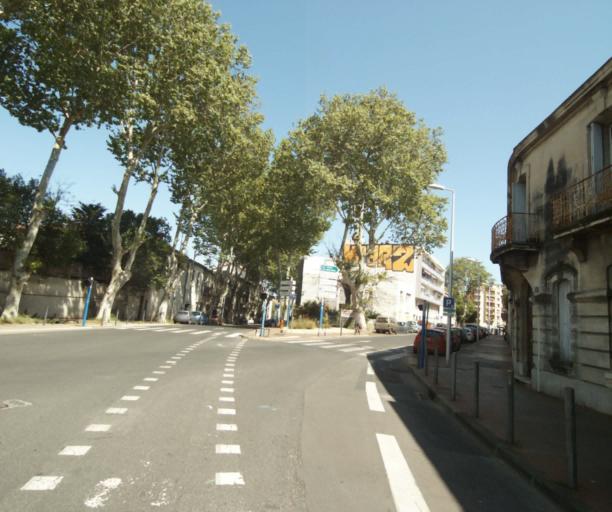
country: FR
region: Languedoc-Roussillon
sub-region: Departement de l'Herault
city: Montpellier
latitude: 43.6015
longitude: 3.8826
